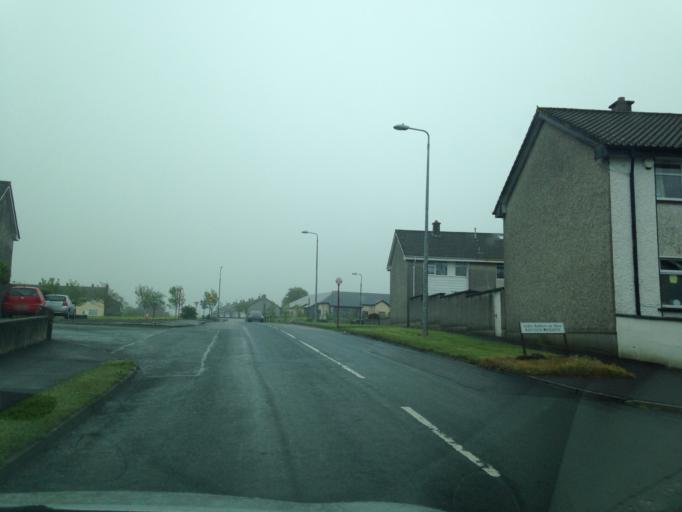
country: IE
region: Connaught
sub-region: County Galway
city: Gaillimh
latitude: 53.2810
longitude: -9.0115
